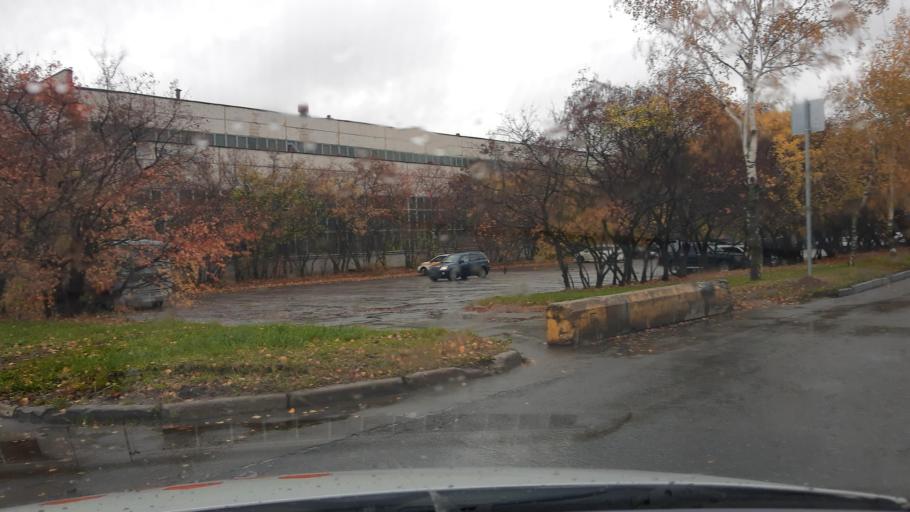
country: RU
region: Moscow
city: Tsaritsyno
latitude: 55.6086
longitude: 37.6531
